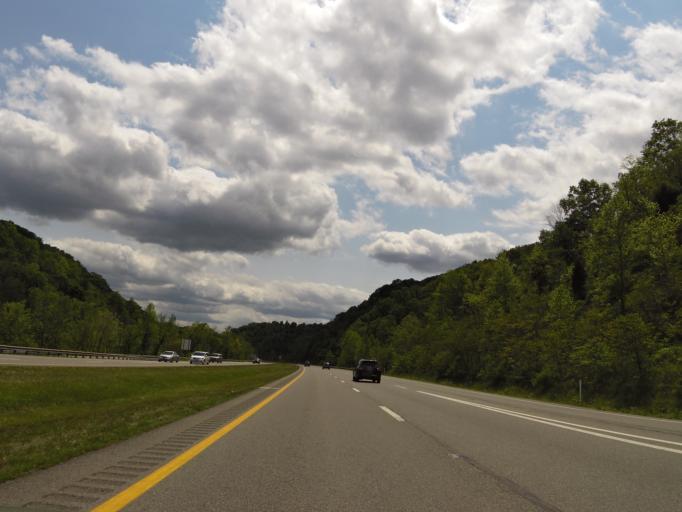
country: US
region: West Virginia
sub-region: Kanawha County
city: Sissonville
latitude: 38.5962
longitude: -81.6412
